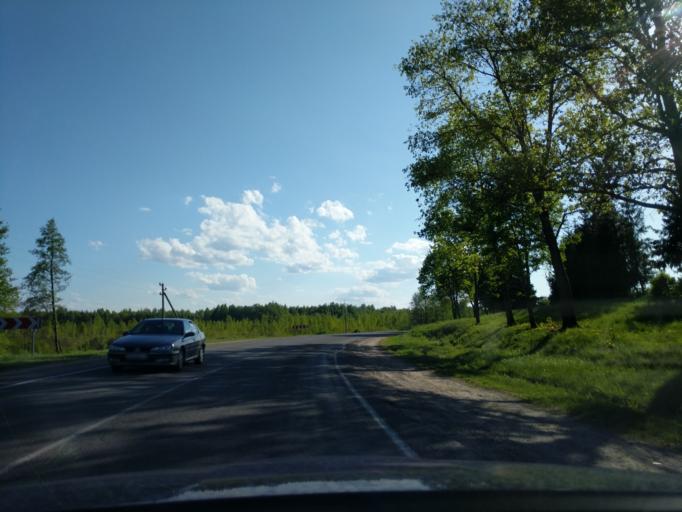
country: BY
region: Minsk
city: Myadzyel
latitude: 54.8605
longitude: 26.9318
